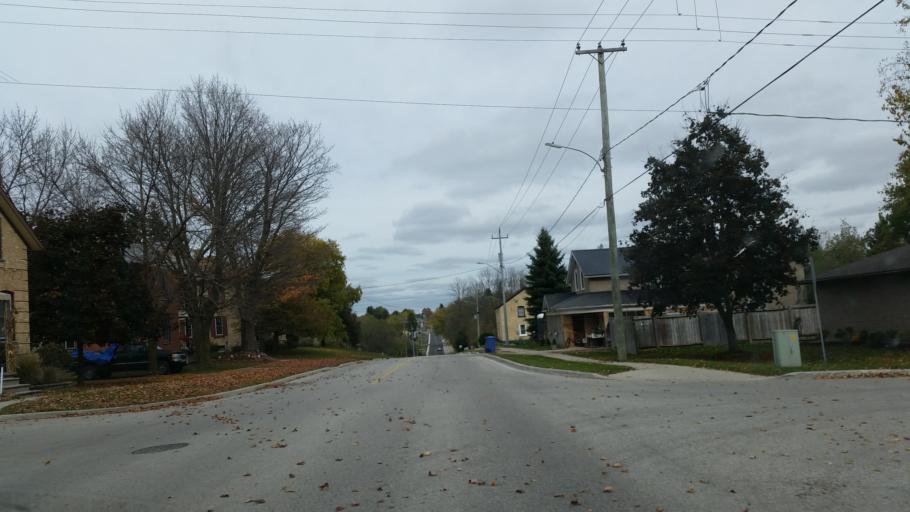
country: CA
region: Ontario
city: Hanover
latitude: 44.0378
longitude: -81.1236
